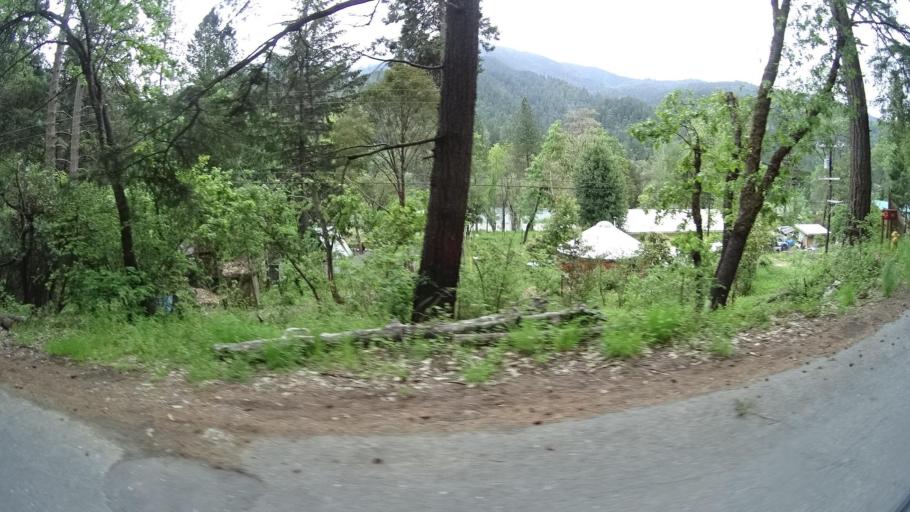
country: US
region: California
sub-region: Humboldt County
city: Willow Creek
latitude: 41.3099
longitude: -123.5314
